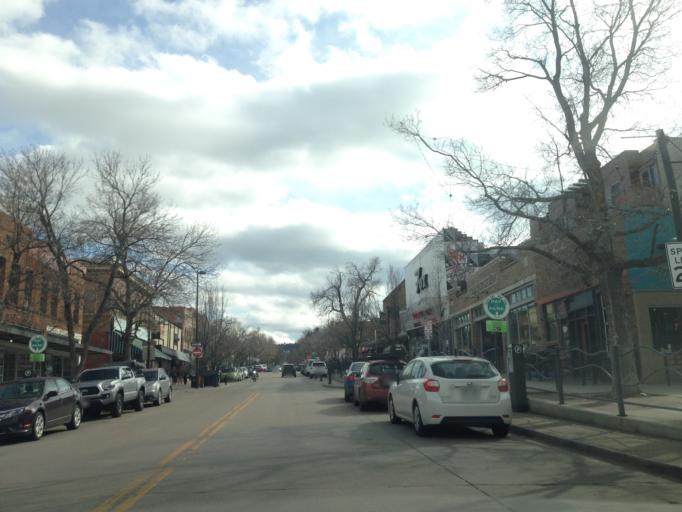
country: US
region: Colorado
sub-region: Boulder County
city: Boulder
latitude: 40.0085
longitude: -105.2762
